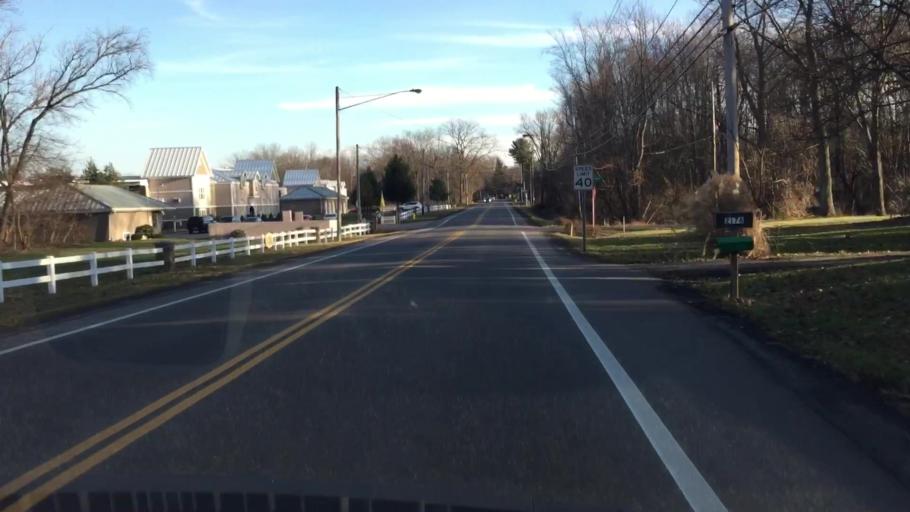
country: US
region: Ohio
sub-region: Summit County
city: Fairlawn
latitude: 41.0859
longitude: -81.5991
